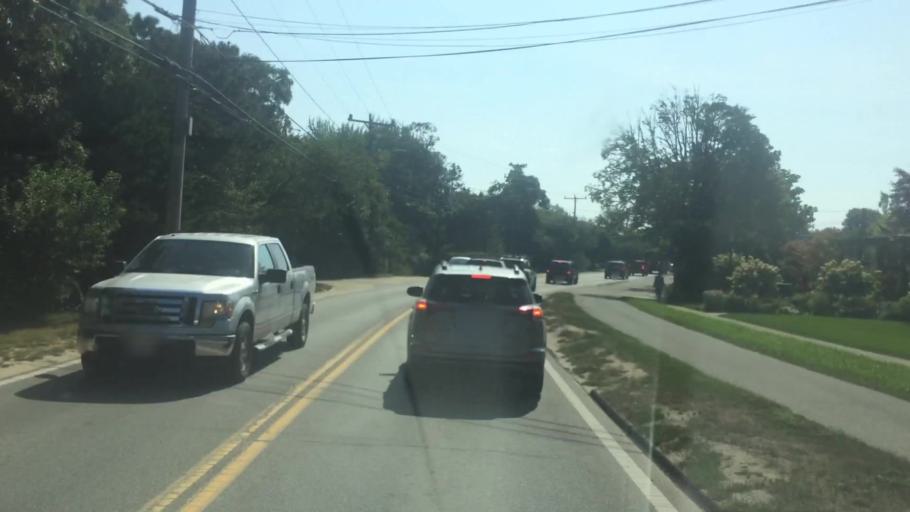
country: US
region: Massachusetts
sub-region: Dukes County
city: Edgartown
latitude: 41.3951
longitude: -70.5285
